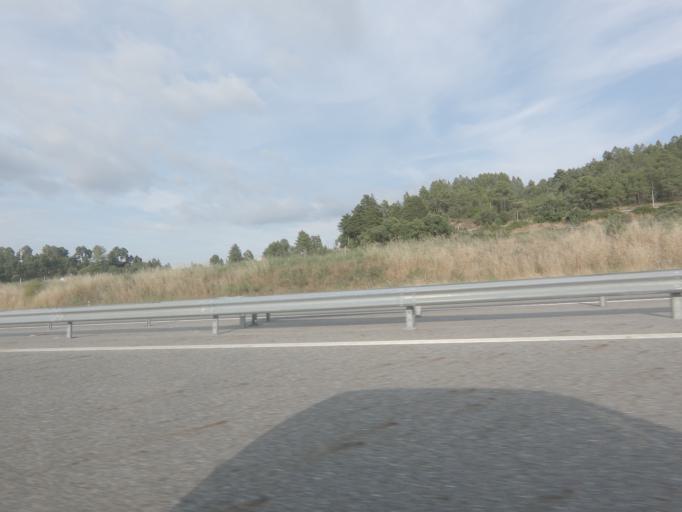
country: PT
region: Vila Real
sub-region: Boticas
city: Boticas
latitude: 41.6552
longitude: -7.5798
